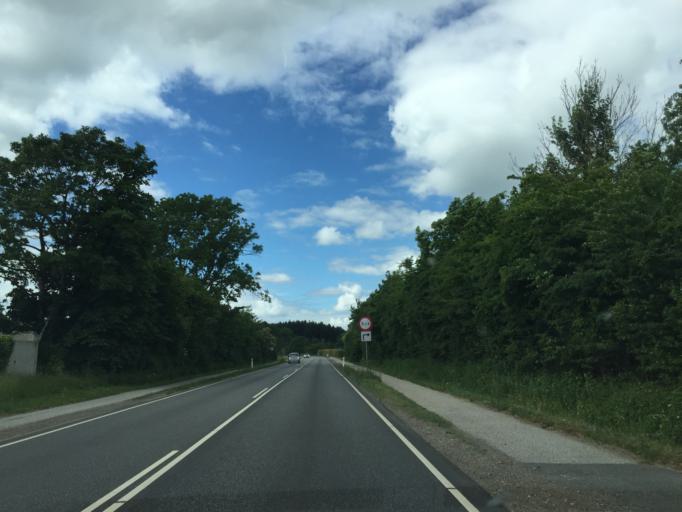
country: DK
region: South Denmark
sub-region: Svendborg Kommune
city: Svendborg
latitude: 55.0734
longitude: 10.5585
